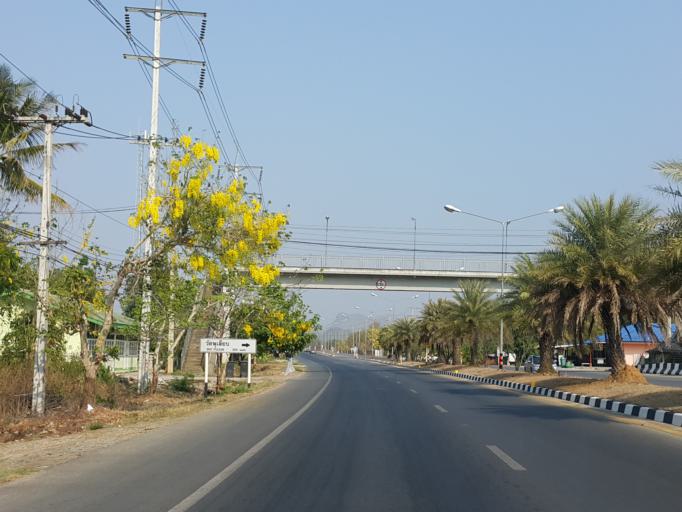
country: TH
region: Kanchanaburi
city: Kanchanaburi
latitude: 14.0667
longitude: 99.4120
